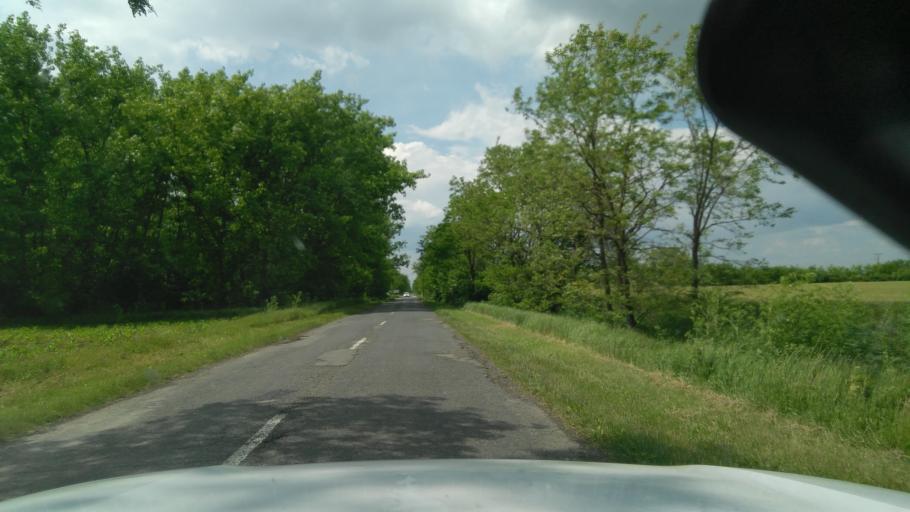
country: HU
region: Bekes
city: Magyarbanhegyes
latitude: 46.4685
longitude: 20.9456
